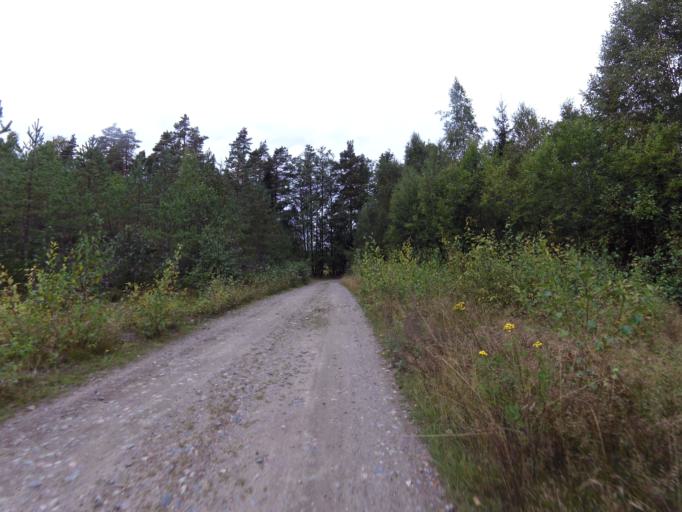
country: SE
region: Gaevleborg
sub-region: Gavle Kommun
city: Valbo
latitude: 60.7506
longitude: 16.9770
